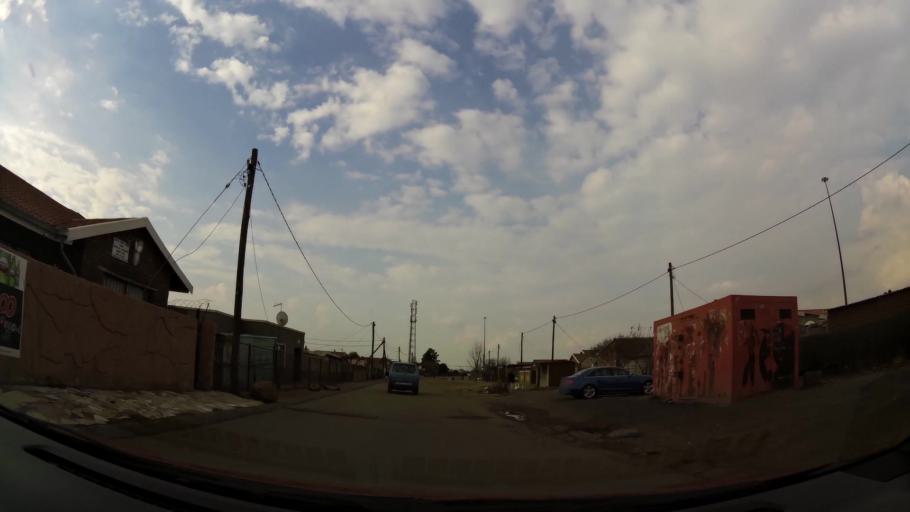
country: ZA
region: Gauteng
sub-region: Sedibeng District Municipality
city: Vanderbijlpark
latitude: -26.6742
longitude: 27.8730
